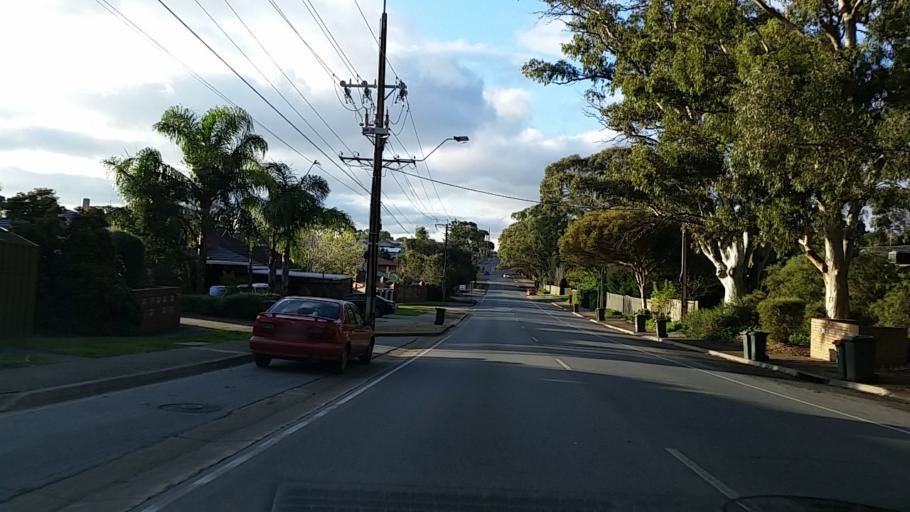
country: AU
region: South Australia
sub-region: Tea Tree Gully
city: Hope Valley
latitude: -34.8510
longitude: 138.7022
